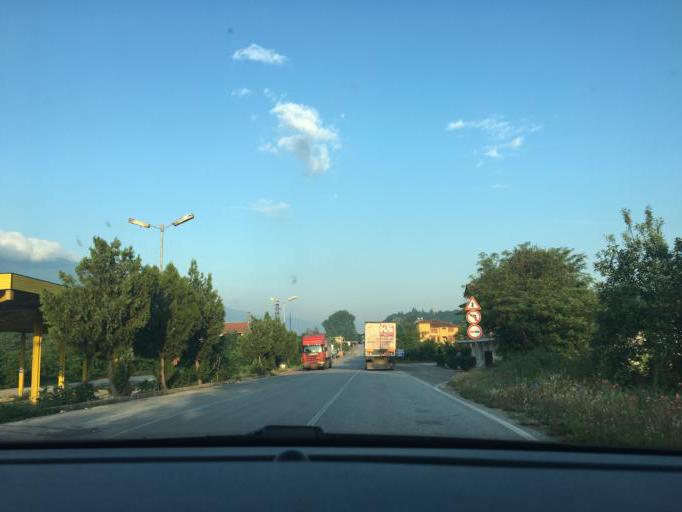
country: MK
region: Novo Selo
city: Novo Selo
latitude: 41.3973
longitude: 22.9741
